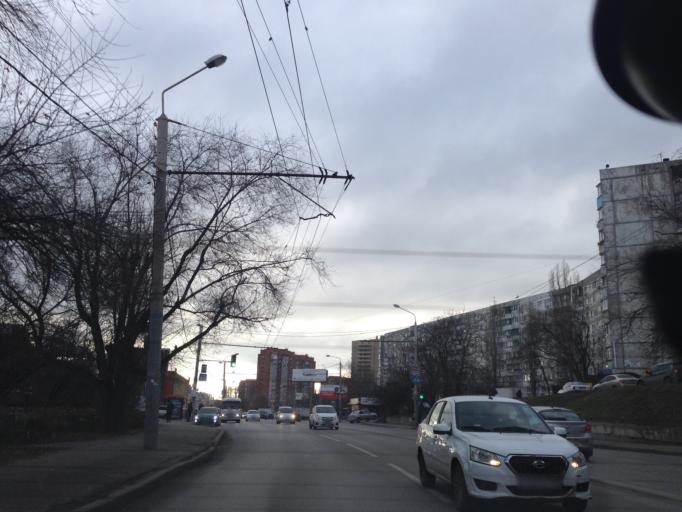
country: RU
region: Rostov
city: Severnyy
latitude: 47.2976
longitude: 39.7229
